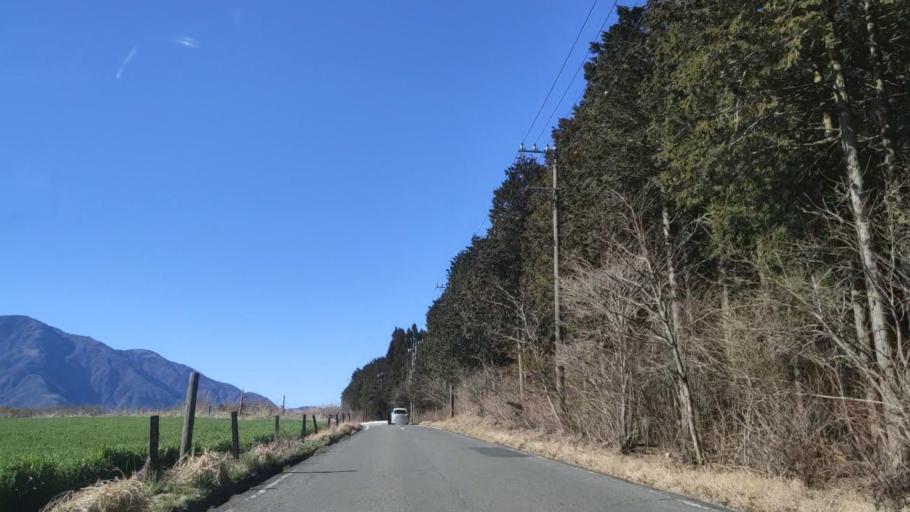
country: JP
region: Yamanashi
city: Fujikawaguchiko
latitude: 35.3792
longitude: 138.6048
